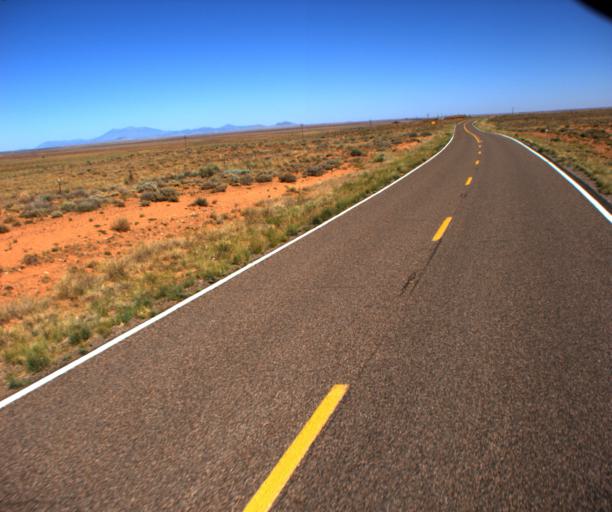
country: US
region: Arizona
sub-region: Coconino County
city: LeChee
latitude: 35.1108
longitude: -110.8676
